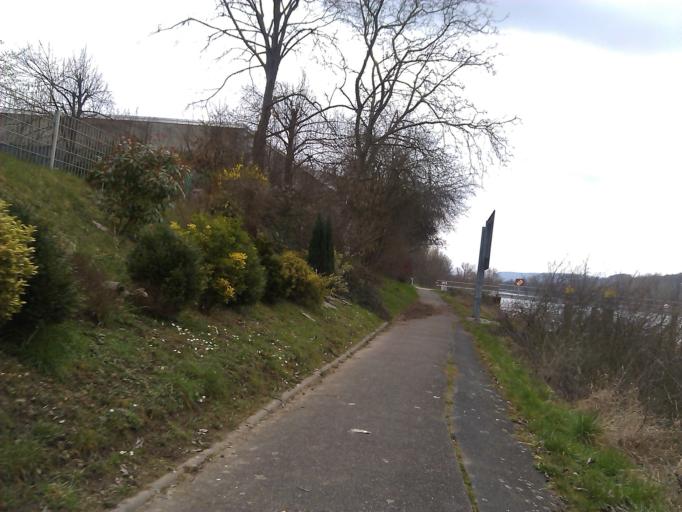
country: DE
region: Rheinland-Pfalz
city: Niederwerth
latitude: 50.3875
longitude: 7.6060
